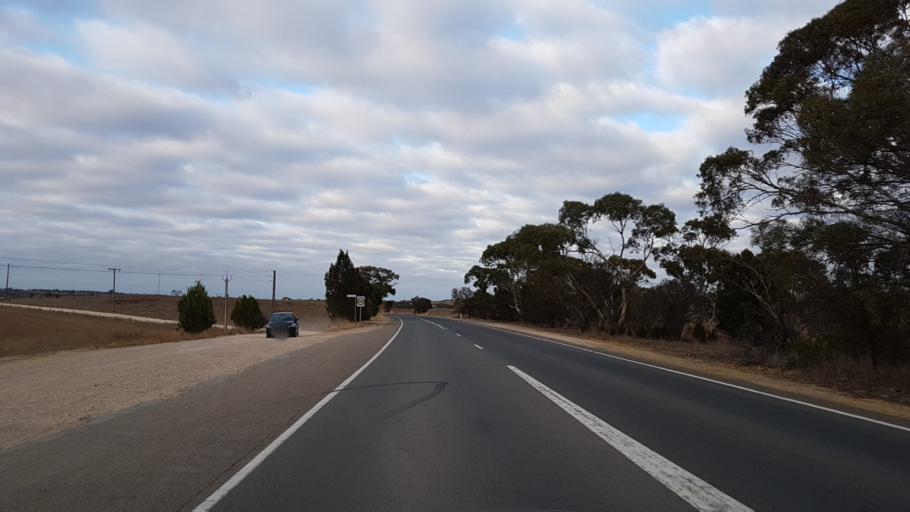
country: AU
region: South Australia
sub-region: Mount Barker
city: Callington
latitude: -35.1307
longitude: 139.0345
